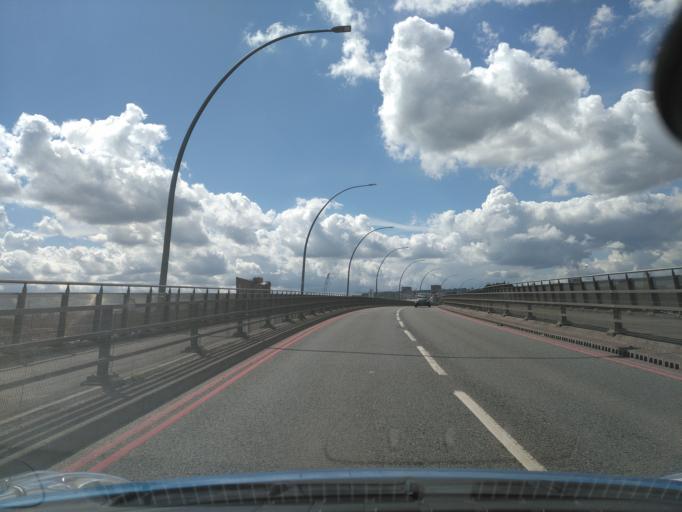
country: GB
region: England
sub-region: Greater London
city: Woolwich
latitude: 51.5064
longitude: 0.0712
